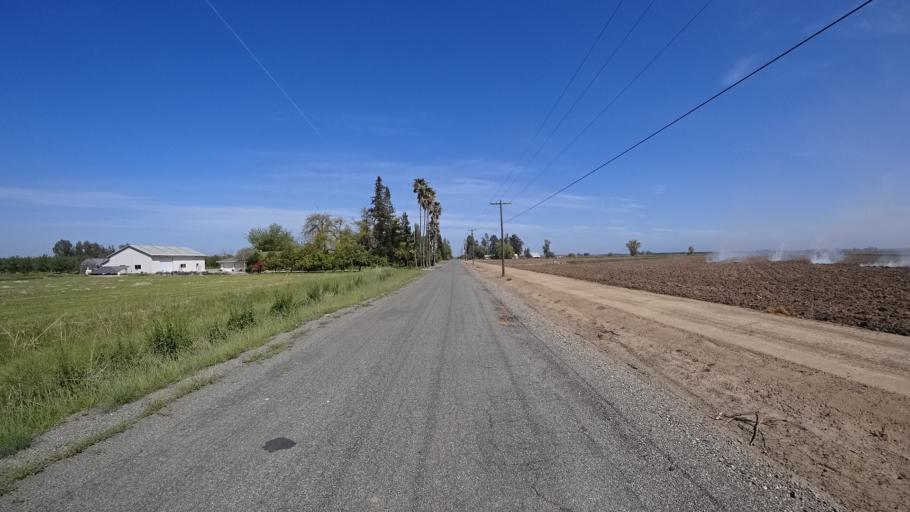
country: US
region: California
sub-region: Glenn County
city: Hamilton City
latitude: 39.5974
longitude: -122.0557
